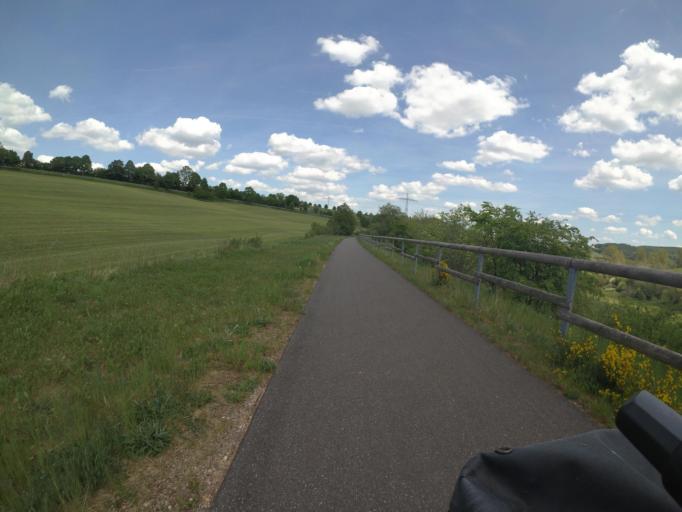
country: DE
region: Rheinland-Pfalz
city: Scheid
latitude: 50.3532
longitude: 6.4233
